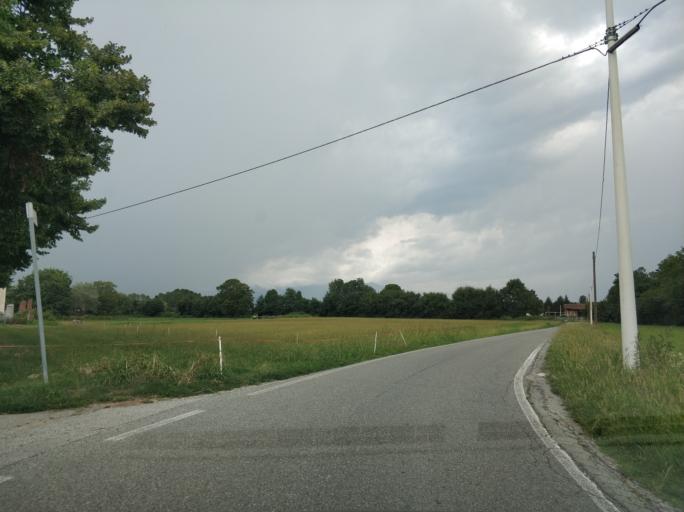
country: IT
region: Piedmont
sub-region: Provincia di Torino
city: Caselle Torinese
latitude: 45.1817
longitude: 7.6253
